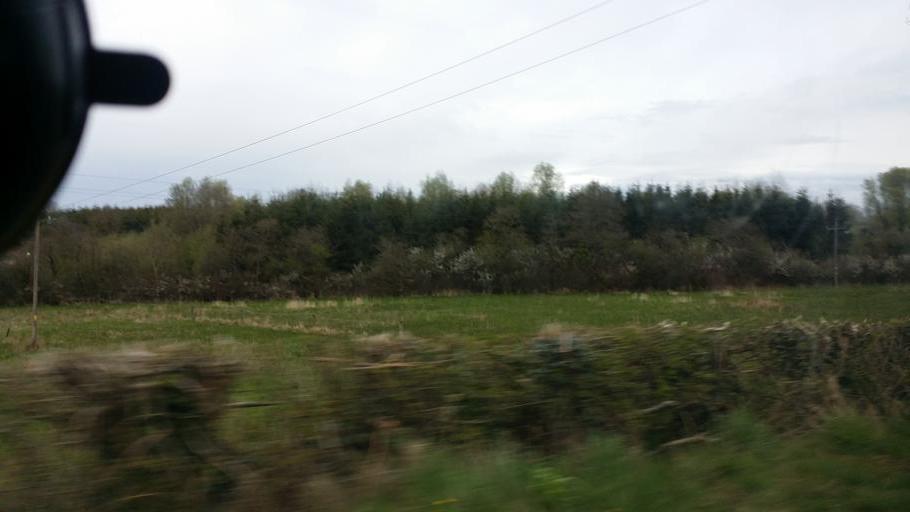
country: IE
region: Ulster
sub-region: An Cabhan
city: Belturbet
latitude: 54.0908
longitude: -7.4971
